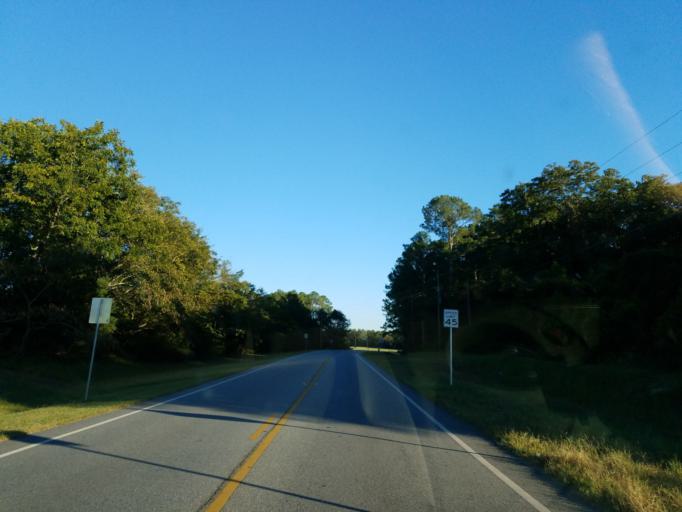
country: US
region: Georgia
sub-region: Worth County
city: Sylvester
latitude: 31.5563
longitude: -83.8454
